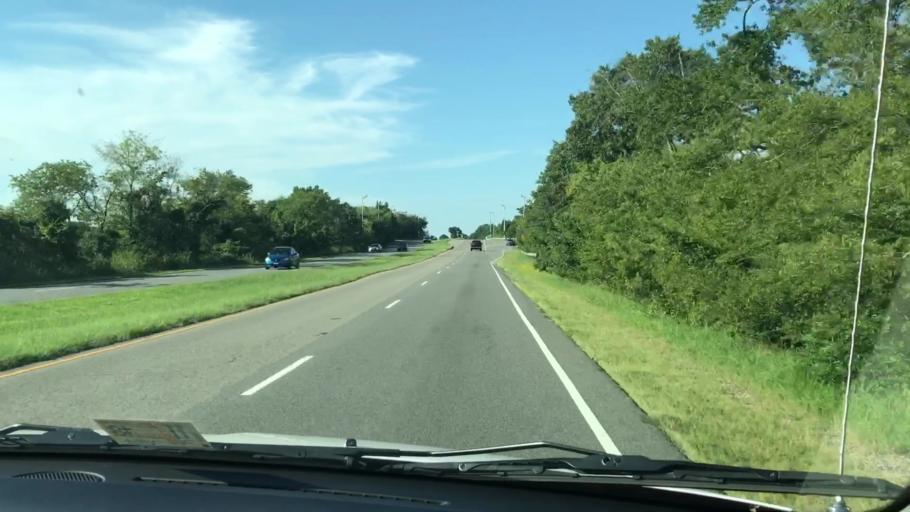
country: US
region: Virginia
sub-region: City of Hampton
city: Hampton
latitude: 37.0402
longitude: -76.3632
